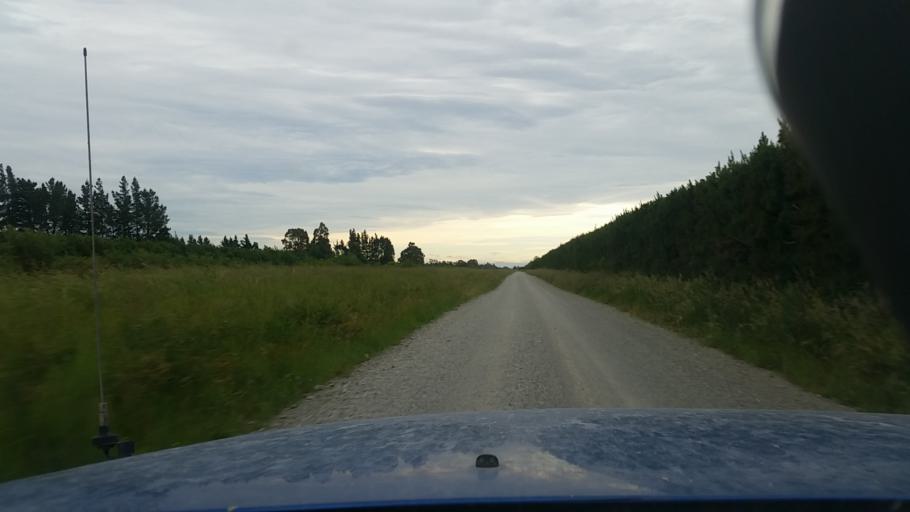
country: NZ
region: Canterbury
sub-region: Ashburton District
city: Tinwald
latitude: -43.9353
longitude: 171.6909
